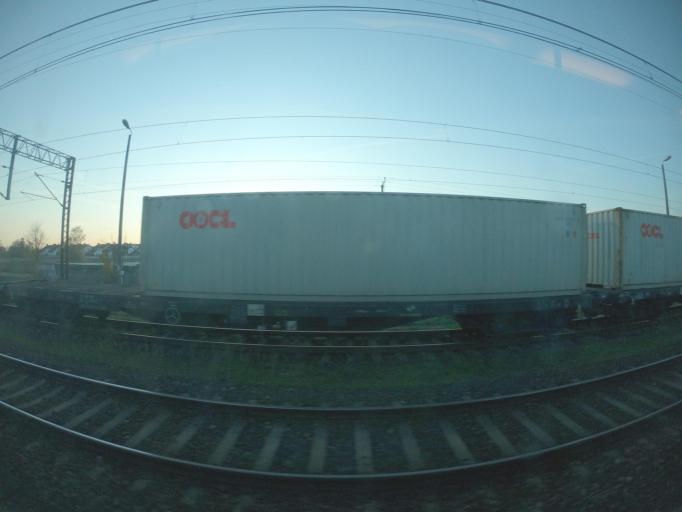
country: PL
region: Lubusz
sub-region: Powiat gorzowski
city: Kostrzyn nad Odra
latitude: 52.6025
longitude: 14.6460
